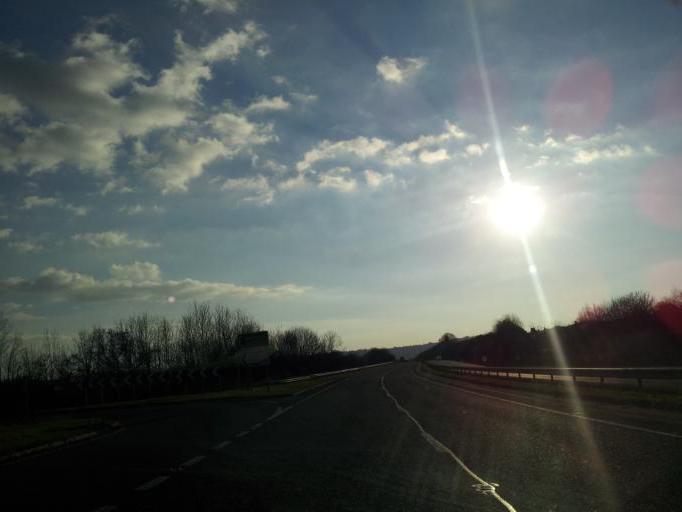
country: GB
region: England
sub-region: Cornwall
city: Launceston
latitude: 50.6453
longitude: -4.3026
